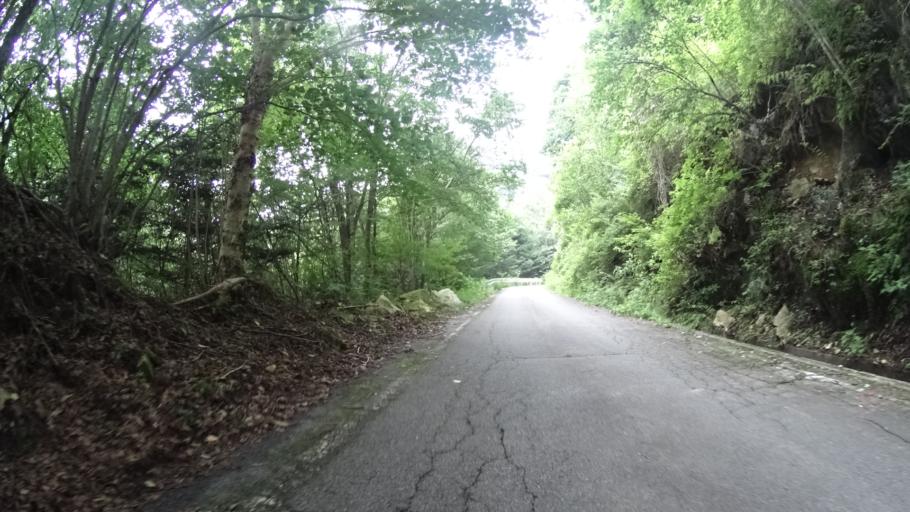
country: JP
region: Yamanashi
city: Kofu-shi
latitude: 35.8083
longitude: 138.6155
